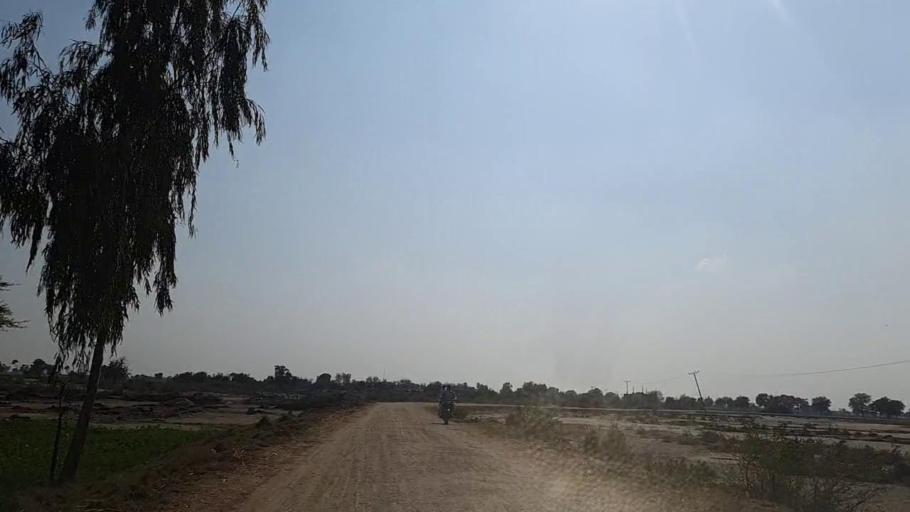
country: PK
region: Sindh
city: Daur
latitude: 26.4552
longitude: 68.2502
